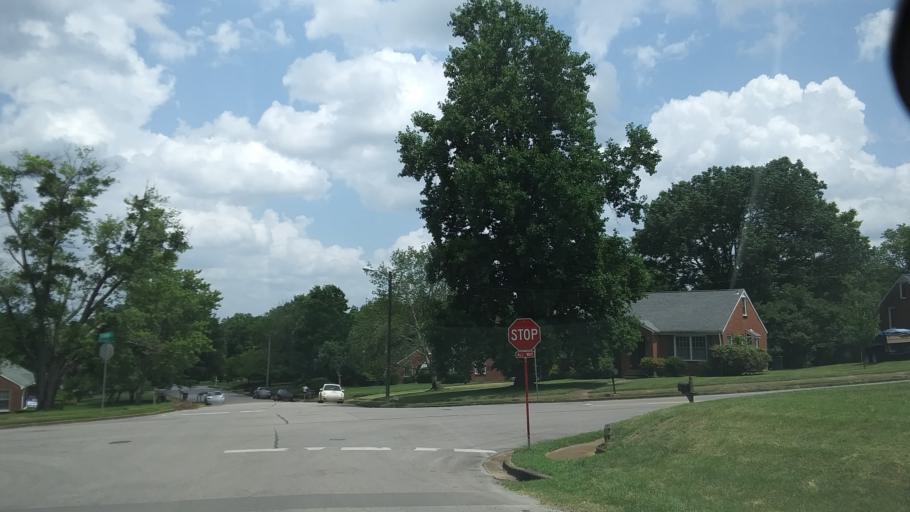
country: US
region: Tennessee
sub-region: Davidson County
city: Belle Meade
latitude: 36.1370
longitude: -86.8618
